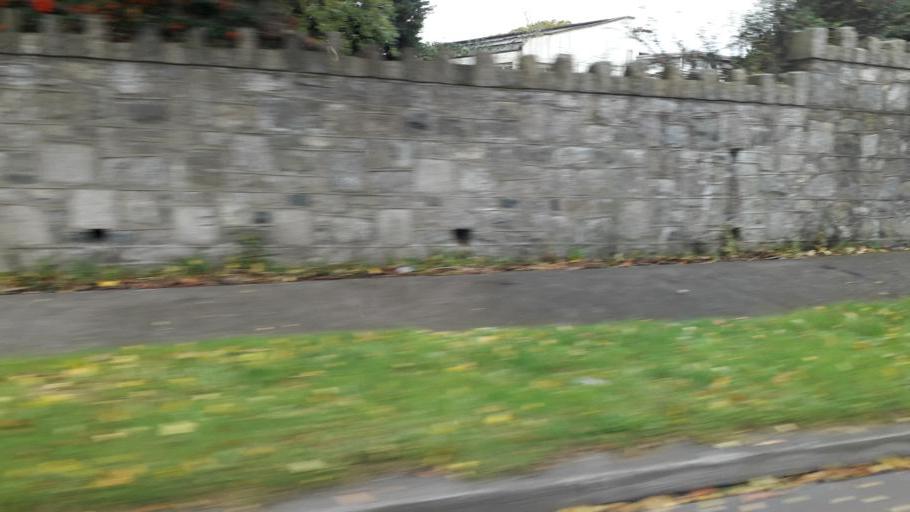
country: IE
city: Clonskeagh
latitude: 53.3162
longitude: -6.2379
